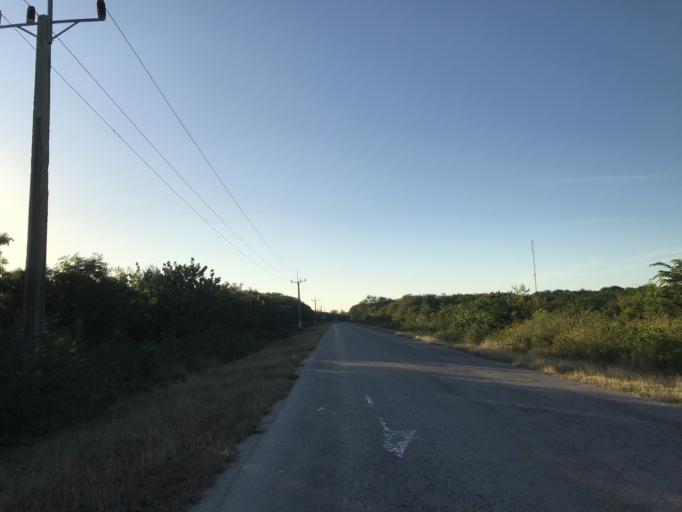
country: CU
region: Cienfuegos
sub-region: Municipio de Aguada de Pasajeros
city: Aguada de Pasajeros
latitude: 22.0669
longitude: -81.0435
